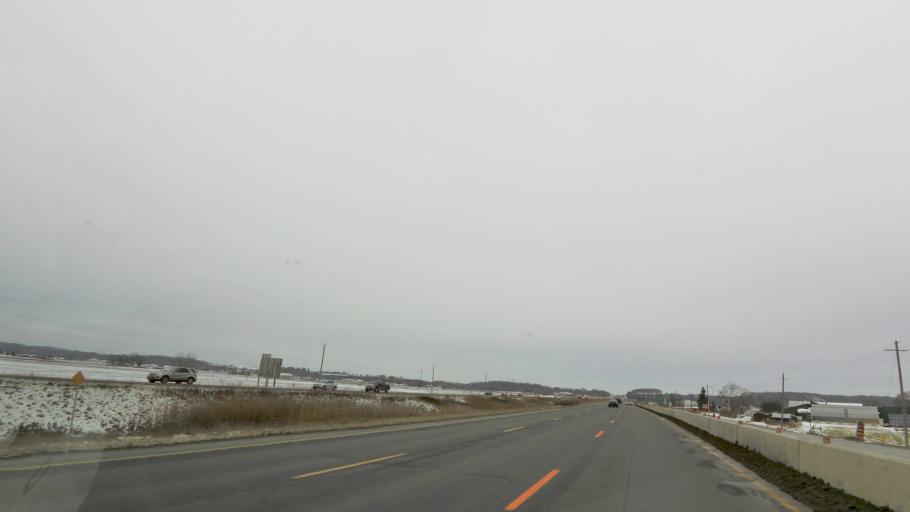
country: CA
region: Ontario
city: Bradford West Gwillimbury
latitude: 44.0397
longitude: -79.5980
